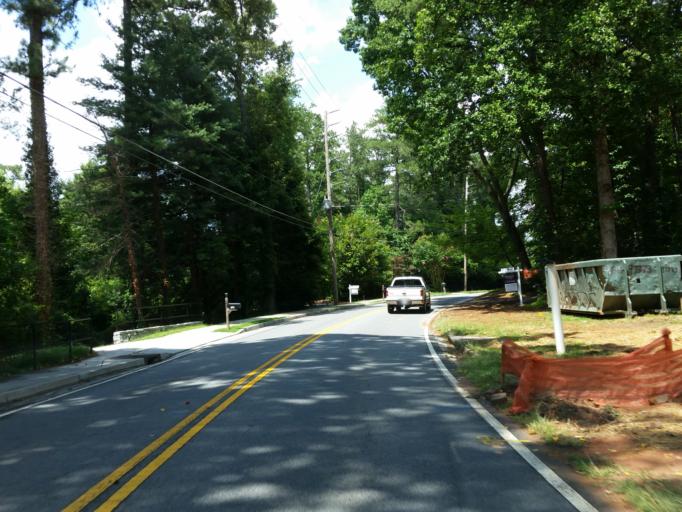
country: US
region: Georgia
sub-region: DeKalb County
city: Dunwoody
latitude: 33.9672
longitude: -84.3463
